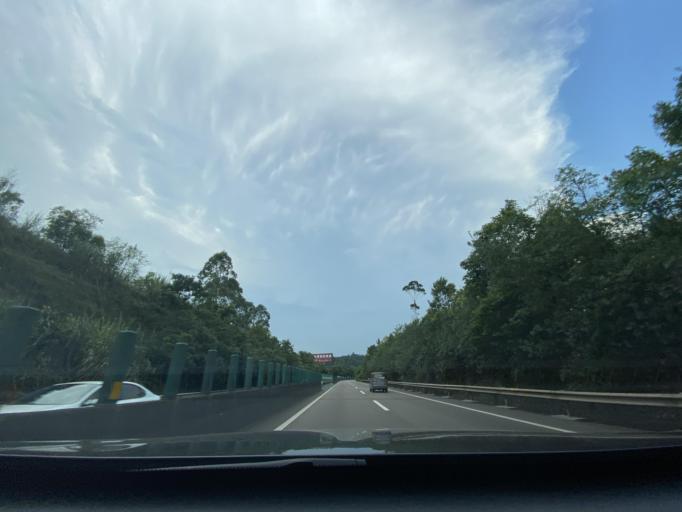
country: CN
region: Sichuan
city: Neijiang
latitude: 29.6320
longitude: 104.9841
